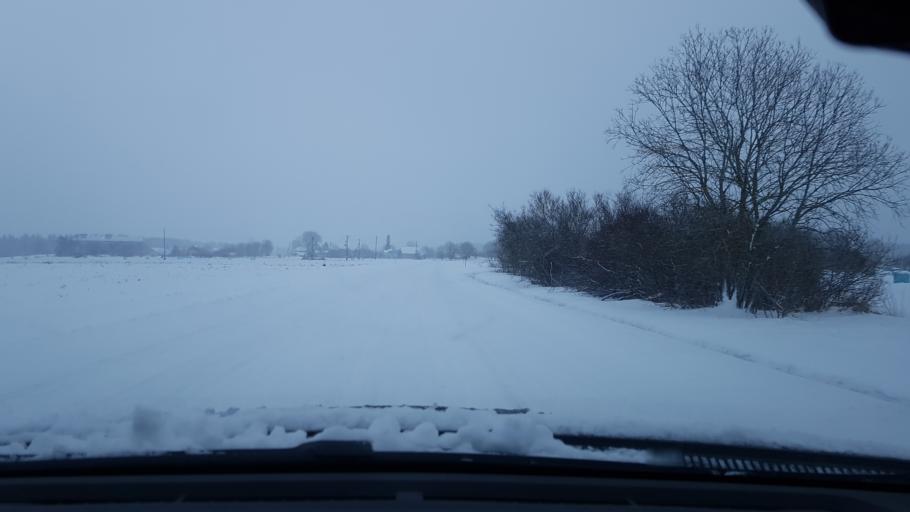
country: EE
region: Harju
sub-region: Kuusalu vald
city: Kuusalu
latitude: 59.4729
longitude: 25.5509
